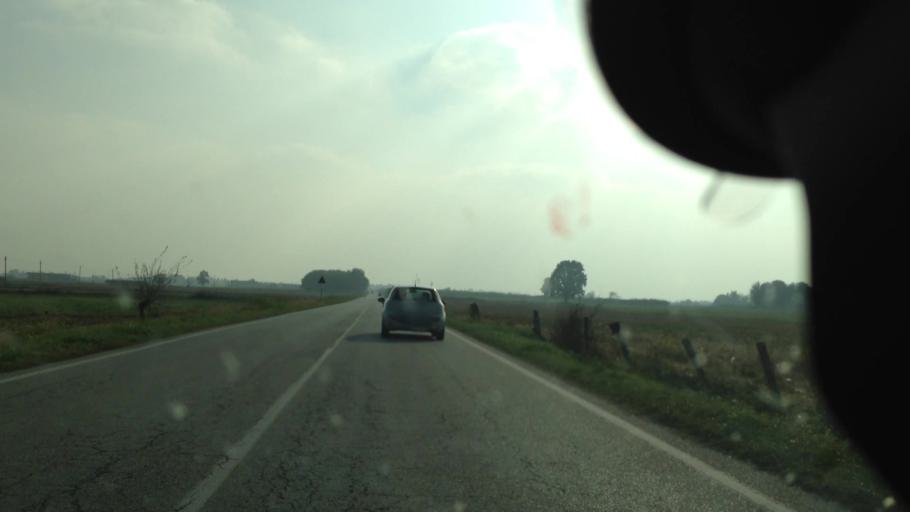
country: IT
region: Piedmont
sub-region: Provincia di Vercelli
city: Borgo d'Ale
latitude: 45.3347
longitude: 8.0420
